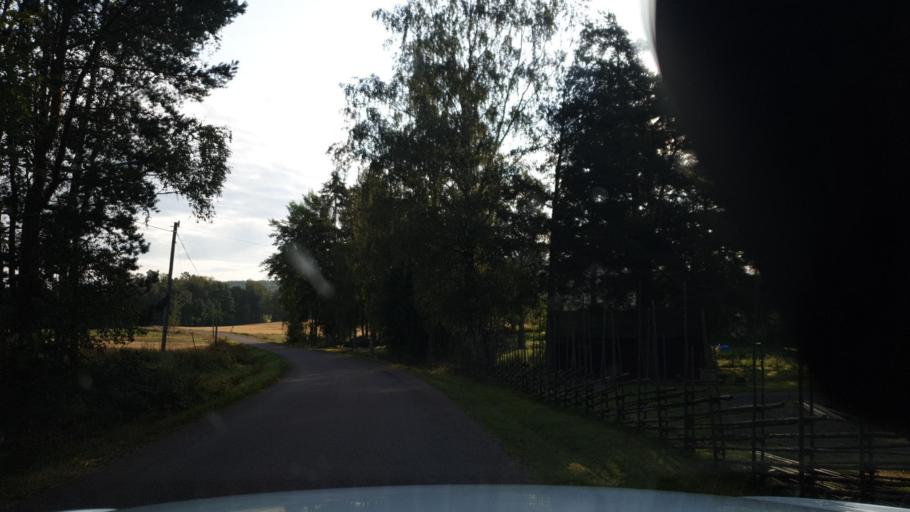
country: SE
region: Vaermland
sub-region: Arvika Kommun
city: Arvika
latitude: 59.7547
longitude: 12.5529
